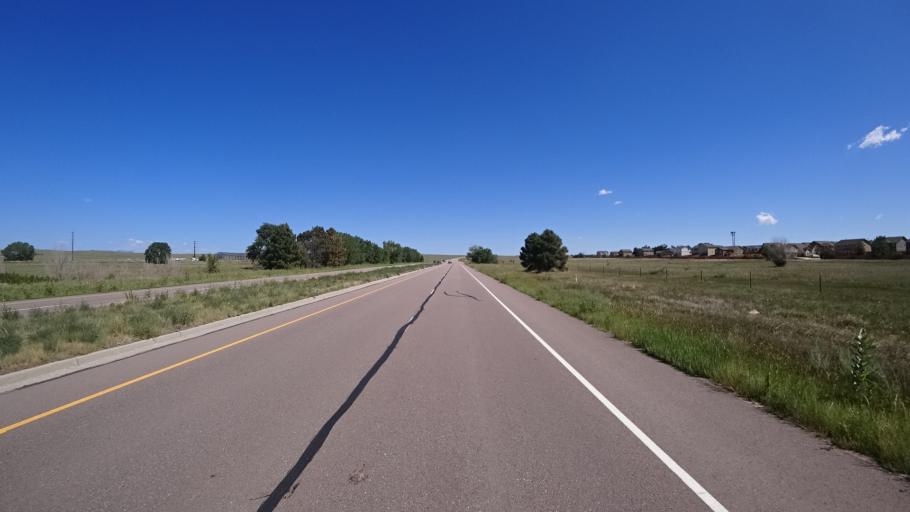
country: US
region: Colorado
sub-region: El Paso County
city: Security-Widefield
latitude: 38.7765
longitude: -104.6596
